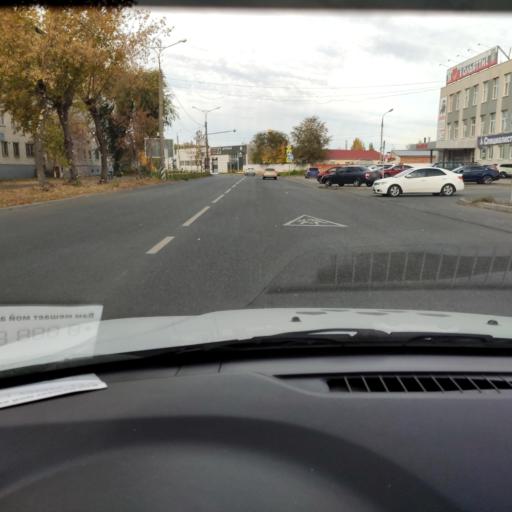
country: RU
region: Samara
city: Tol'yatti
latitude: 53.5285
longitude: 49.4306
